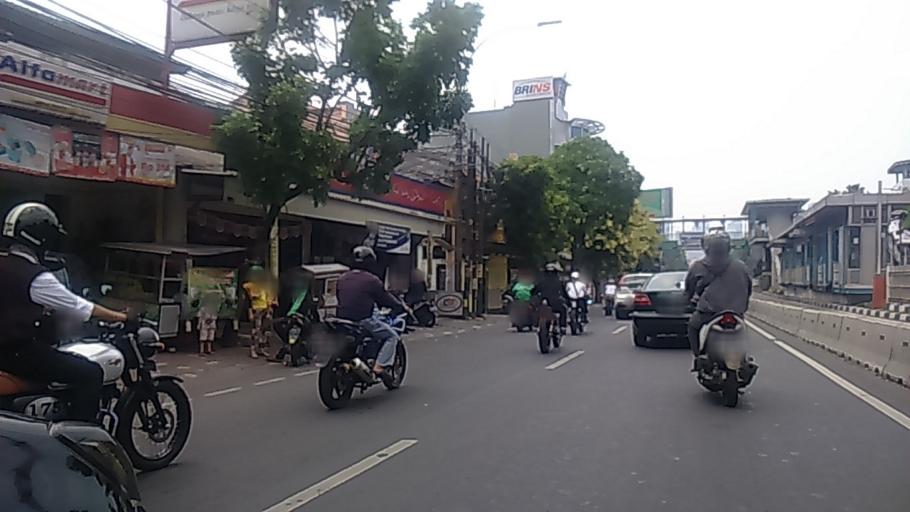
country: ID
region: Jakarta Raya
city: Jakarta
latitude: -6.2535
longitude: 106.8271
